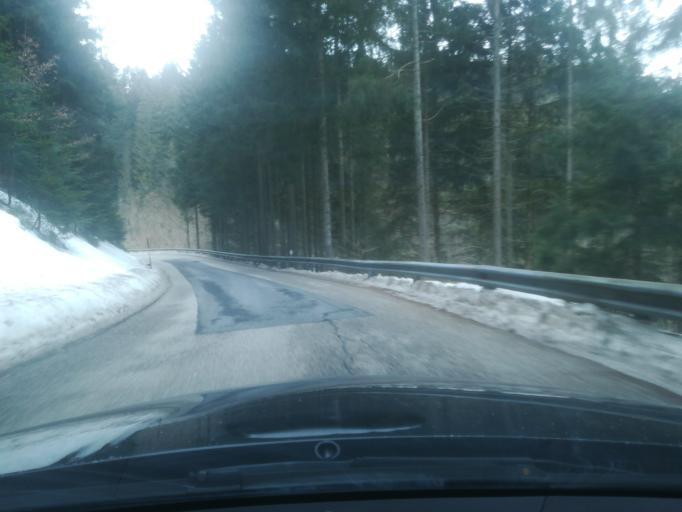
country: AT
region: Upper Austria
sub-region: Politischer Bezirk Perg
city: Perg
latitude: 48.3744
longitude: 14.6296
